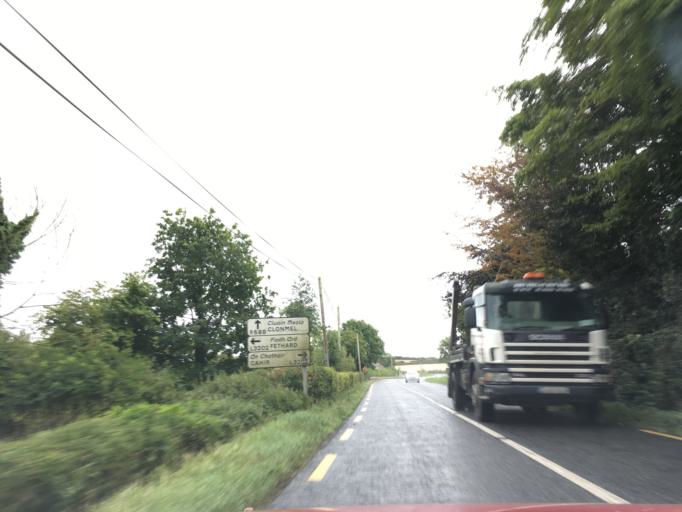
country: IE
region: Munster
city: Fethard
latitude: 52.4242
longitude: -7.7726
